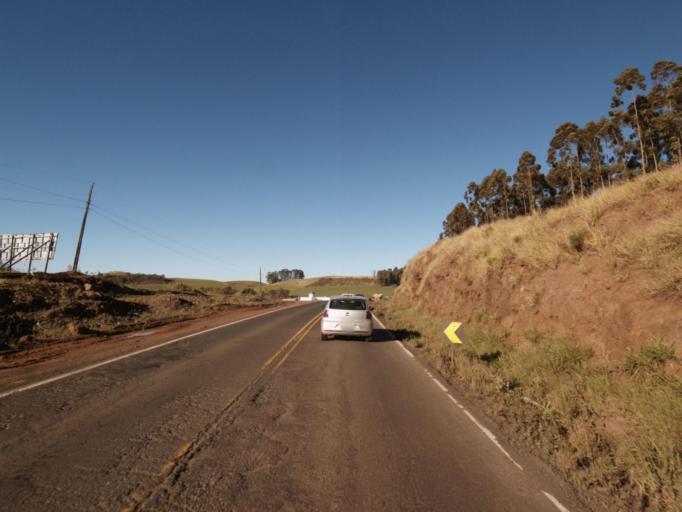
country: AR
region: Misiones
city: Bernardo de Irigoyen
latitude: -26.6261
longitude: -53.5159
